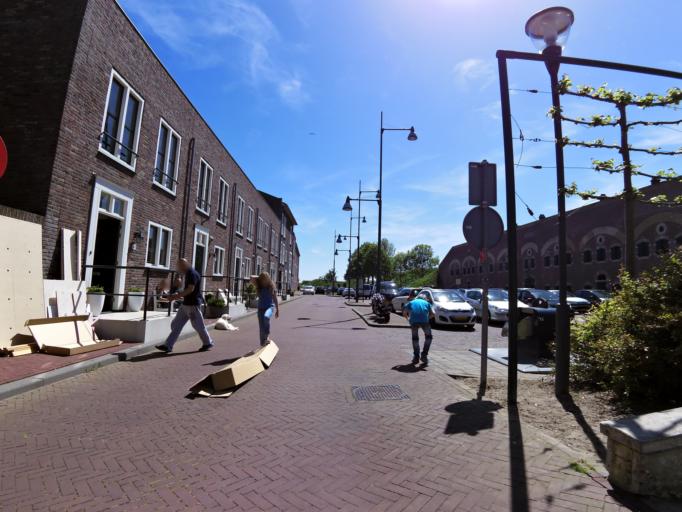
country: NL
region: South Holland
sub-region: Gemeente Hellevoetsluis
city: Hellevoetsluis
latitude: 51.8238
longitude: 4.1274
